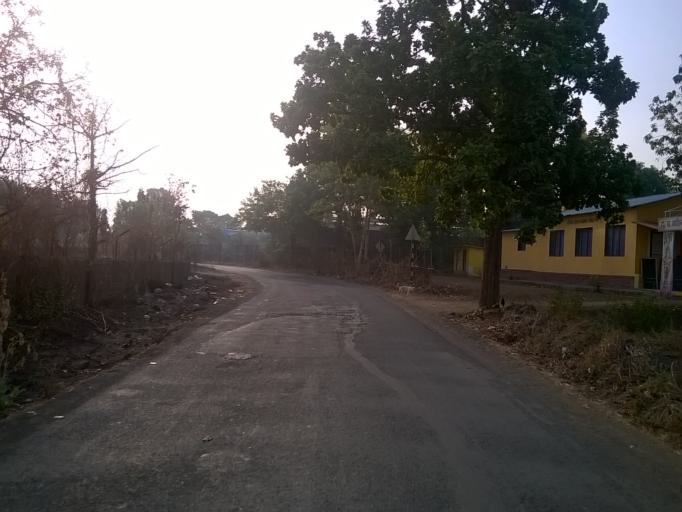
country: IN
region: Maharashtra
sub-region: Raigarh
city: Kalundri
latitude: 19.0150
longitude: 73.1750
